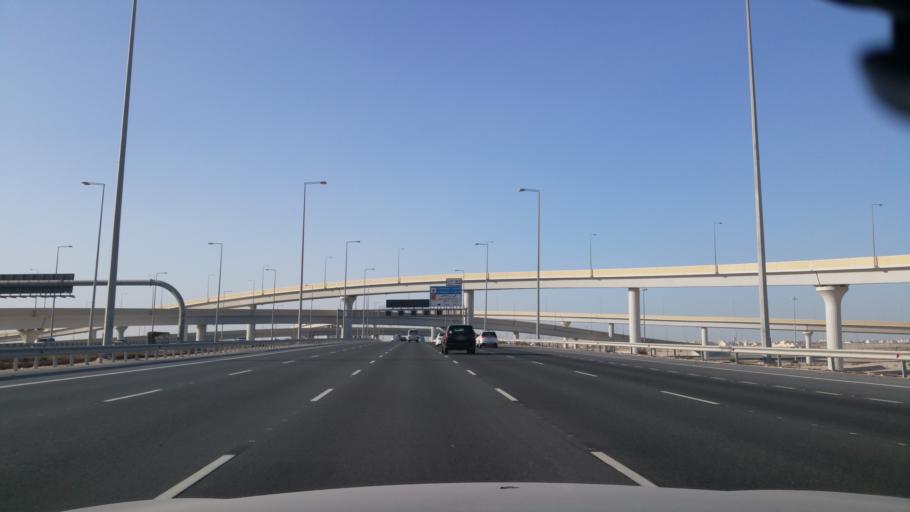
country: QA
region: Al Wakrah
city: Al Wukayr
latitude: 25.2006
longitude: 51.5425
